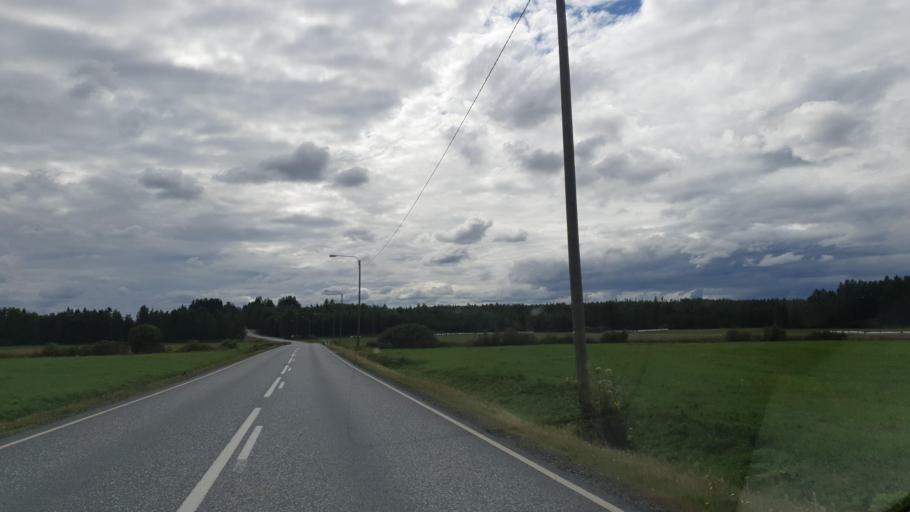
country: FI
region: Northern Savo
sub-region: Ylae-Savo
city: Iisalmi
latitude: 63.5195
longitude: 27.1350
